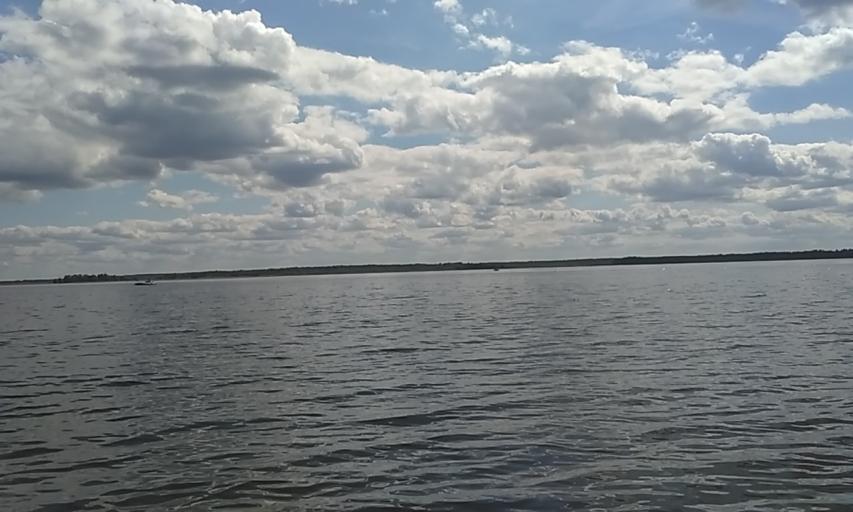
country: BY
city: Novolukoml'
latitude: 54.5902
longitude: 29.1600
